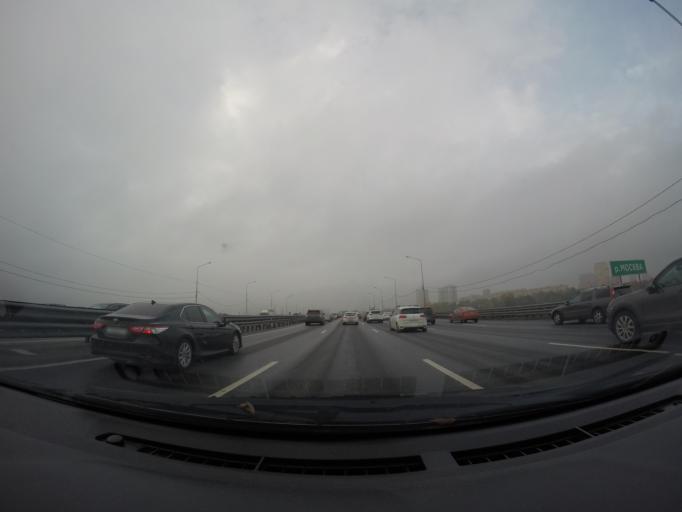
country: RU
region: Moskovskaya
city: Krasnogorsk
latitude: 55.8030
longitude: 37.3301
